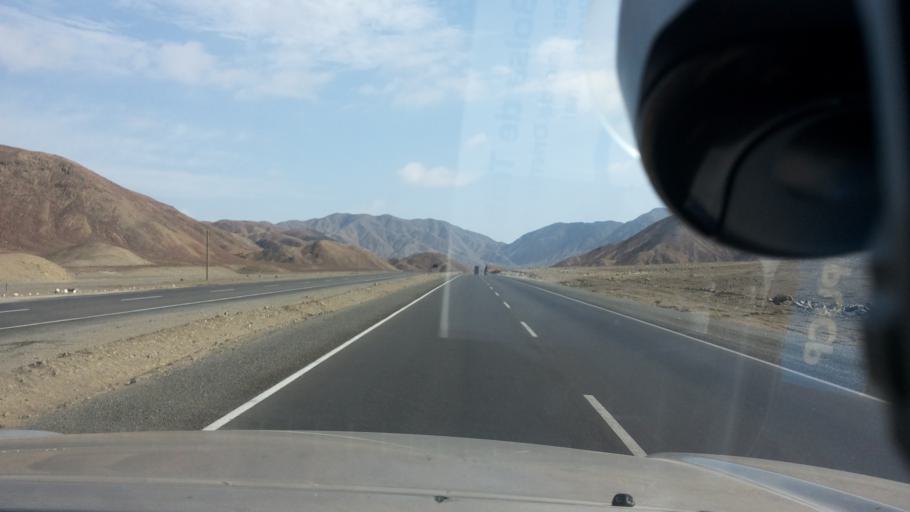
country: PE
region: Ancash
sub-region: Provincia de Huarmey
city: La Caleta Culebras
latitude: -9.8333
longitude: -78.1838
